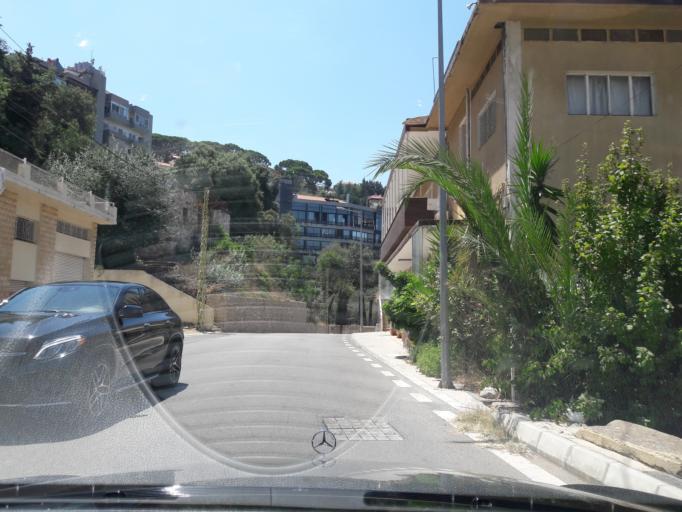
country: LB
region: Mont-Liban
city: Djounie
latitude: 33.9202
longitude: 35.6396
